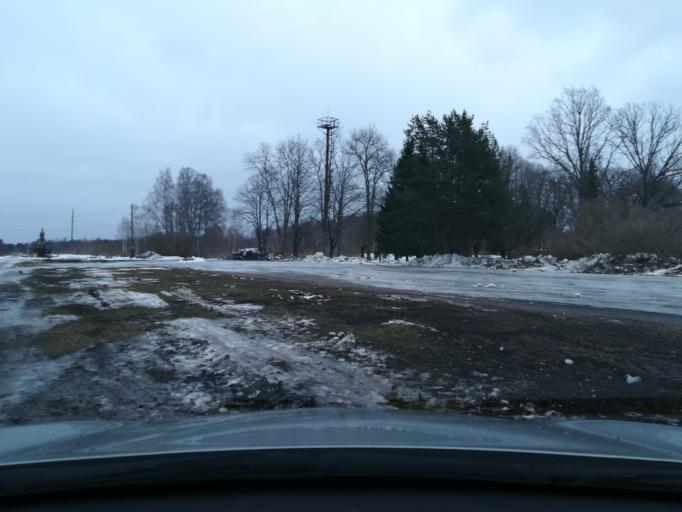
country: EE
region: Harju
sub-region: Nissi vald
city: Turba
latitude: 59.0761
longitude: 24.2405
